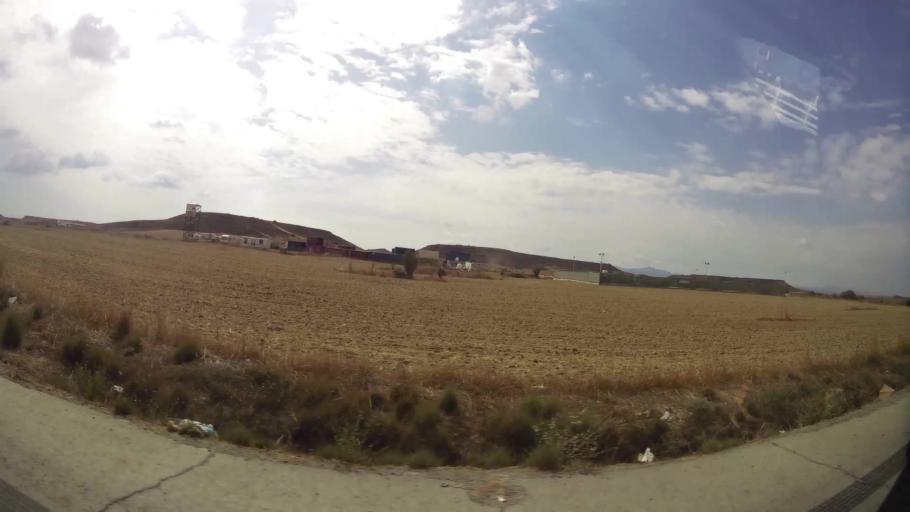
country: CY
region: Lefkosia
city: Tseri
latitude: 35.0588
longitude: 33.3684
